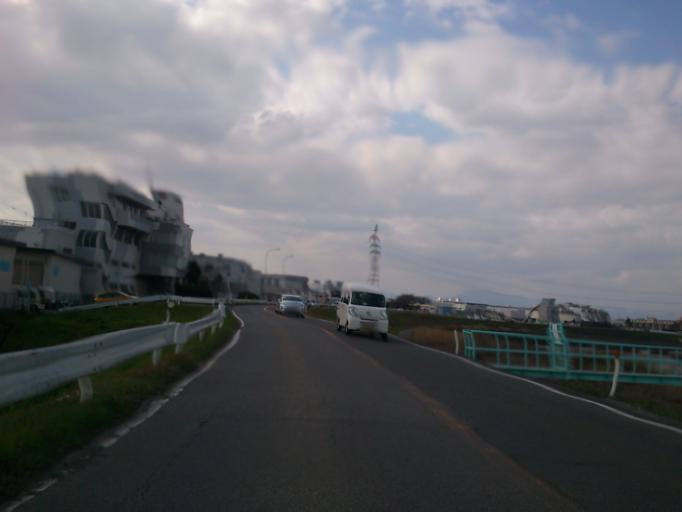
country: JP
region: Kyoto
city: Uji
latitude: 34.9061
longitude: 135.7919
